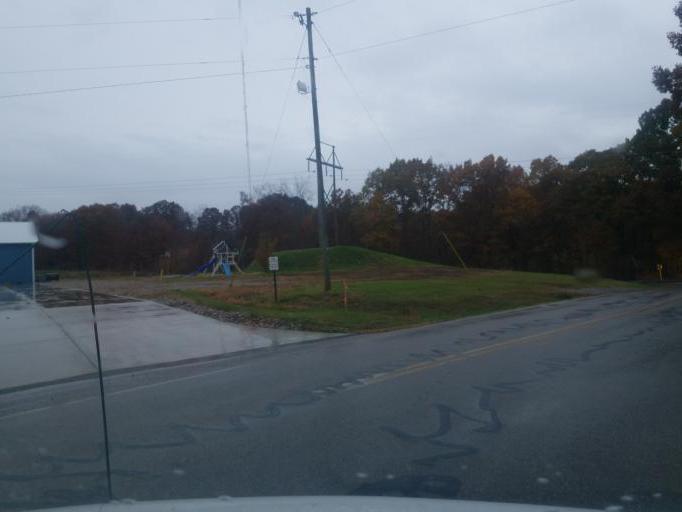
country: US
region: West Virginia
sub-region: Wood County
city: Blennerhassett
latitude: 39.3225
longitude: -81.6216
